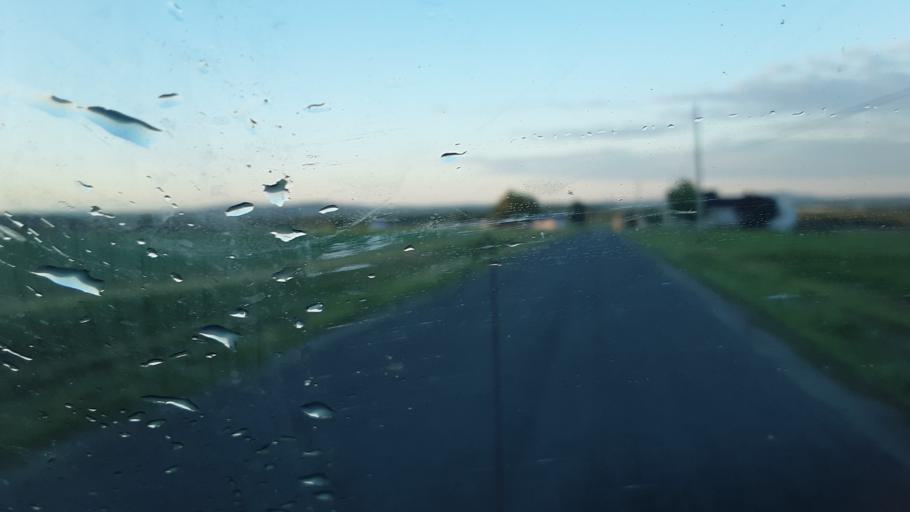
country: US
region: Maine
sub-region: Aroostook County
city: Caribou
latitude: 46.8096
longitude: -68.1351
